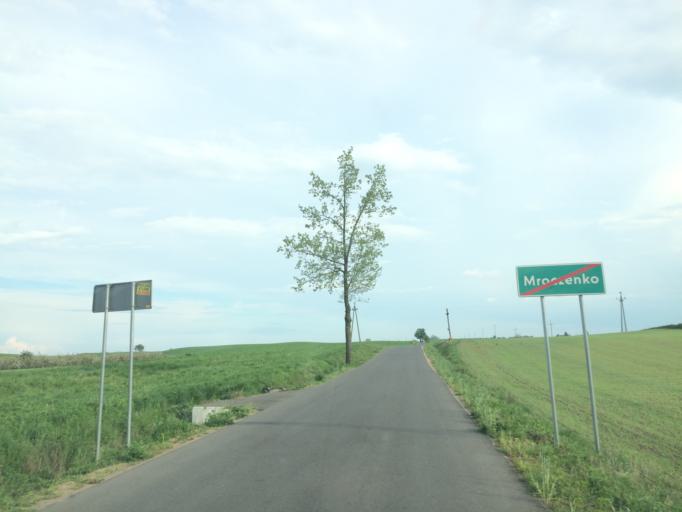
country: PL
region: Warmian-Masurian Voivodeship
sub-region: Powiat nowomiejski
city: Nowe Miasto Lubawskie
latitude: 53.3849
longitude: 19.7048
